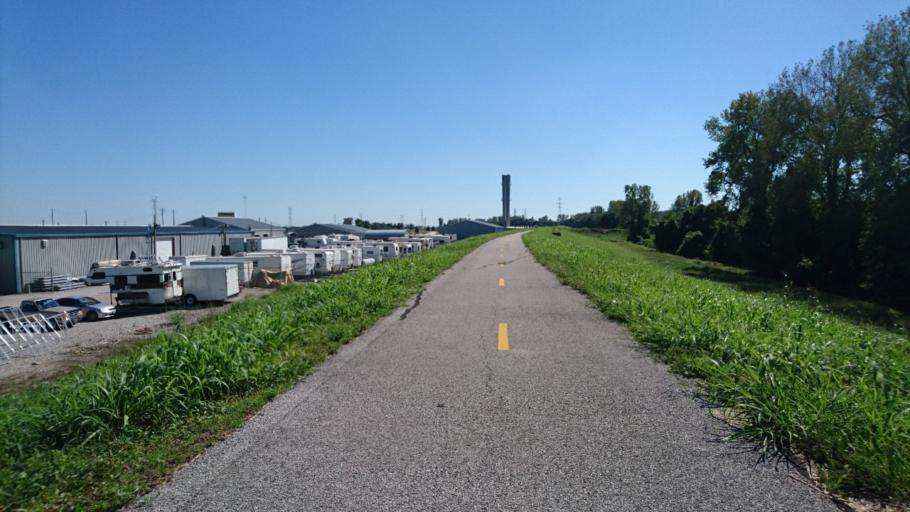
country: US
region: Illinois
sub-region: Madison County
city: Hartford
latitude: 38.8164
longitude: -90.0998
